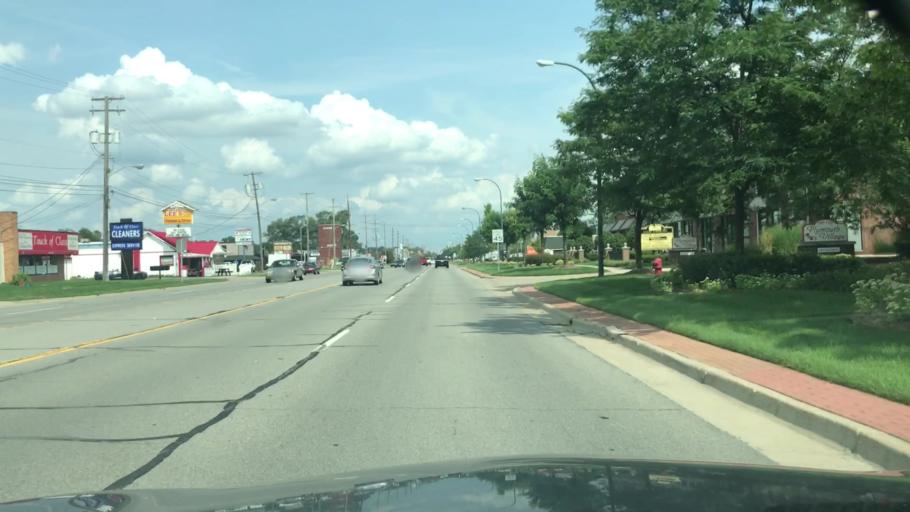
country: US
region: Michigan
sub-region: Wayne County
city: Plymouth
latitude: 42.3585
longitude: -83.4746
